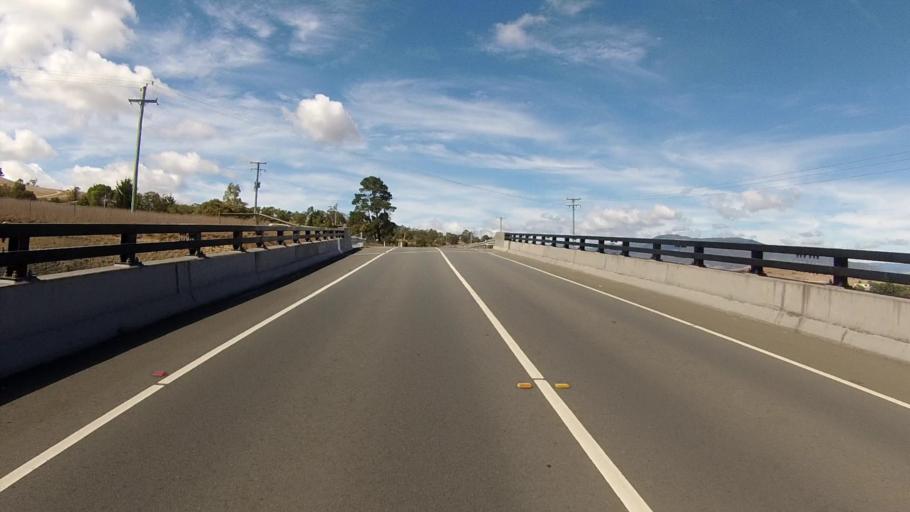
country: AU
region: Tasmania
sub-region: Brighton
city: Bridgewater
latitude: -42.7031
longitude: 147.2710
